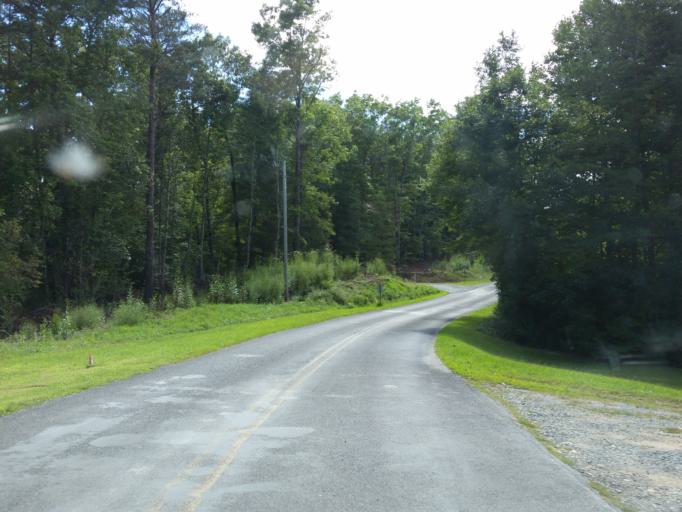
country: US
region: Georgia
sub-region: Fannin County
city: Blue Ridge
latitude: 34.8649
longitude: -84.2382
